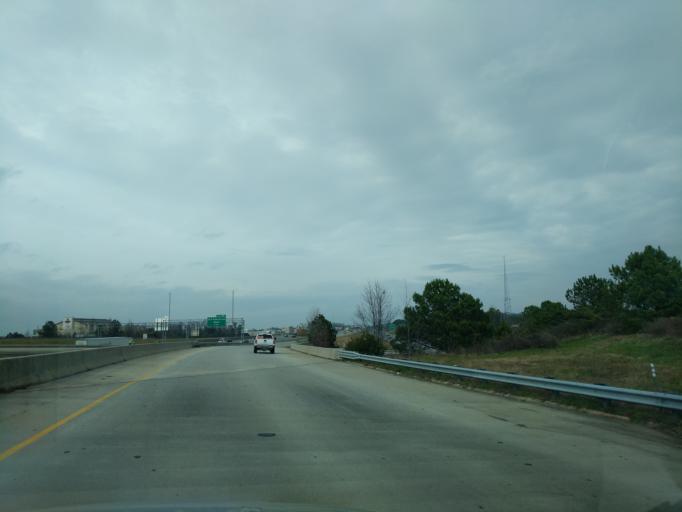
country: US
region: Georgia
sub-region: Gwinnett County
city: Duluth
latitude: 33.9791
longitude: -84.0866
